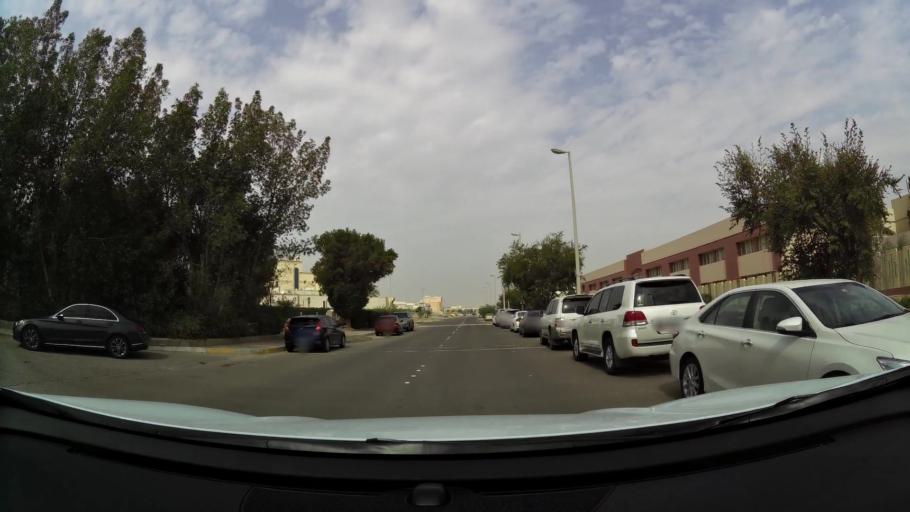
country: AE
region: Abu Dhabi
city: Abu Dhabi
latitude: 24.3252
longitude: 54.6304
